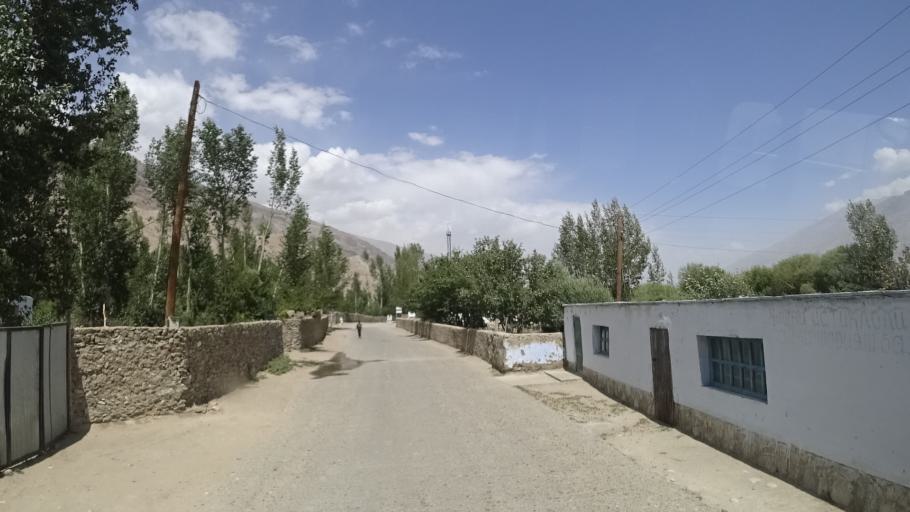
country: AF
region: Badakhshan
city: Khandud
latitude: 36.9209
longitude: 72.1918
